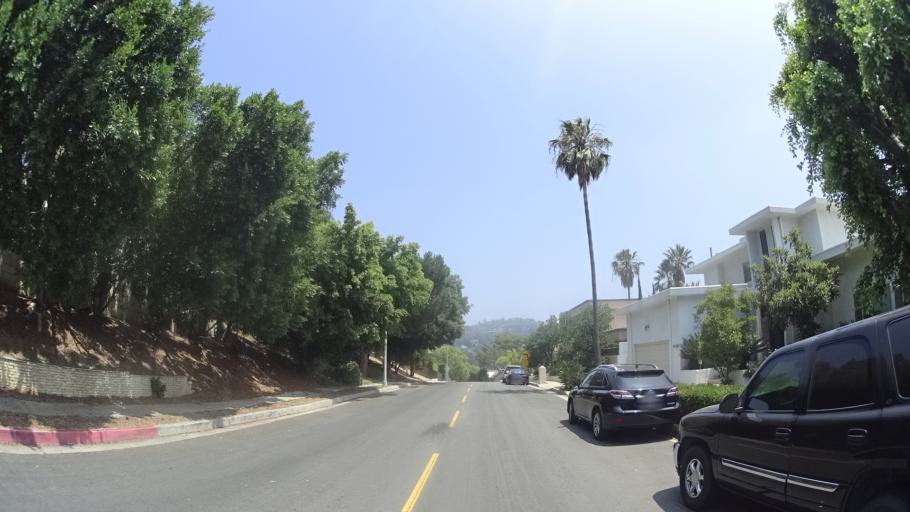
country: US
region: California
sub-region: Los Angeles County
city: West Hollywood
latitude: 34.1135
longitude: -118.3631
